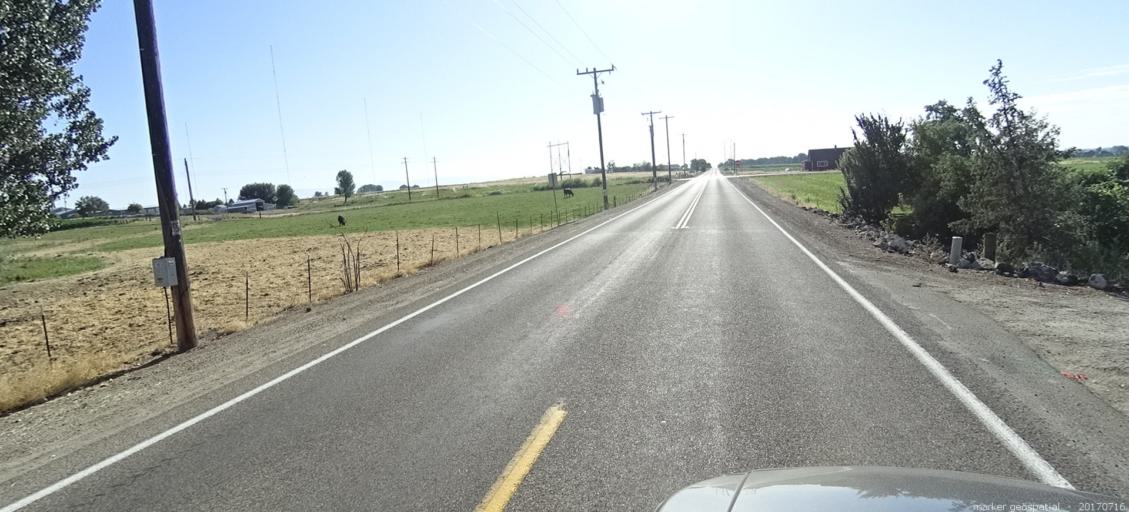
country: US
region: Idaho
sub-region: Ada County
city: Kuna
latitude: 43.5465
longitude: -116.4156
